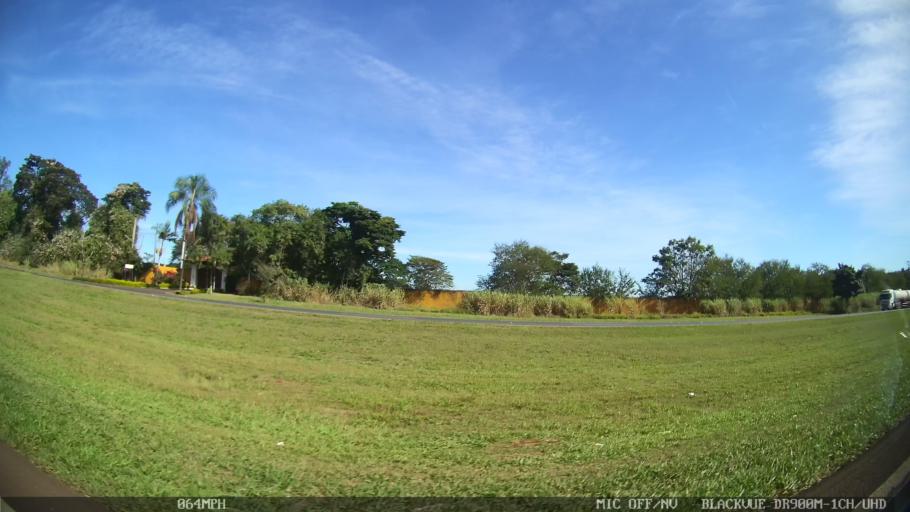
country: BR
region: Sao Paulo
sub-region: Leme
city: Leme
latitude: -22.2364
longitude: -47.3909
